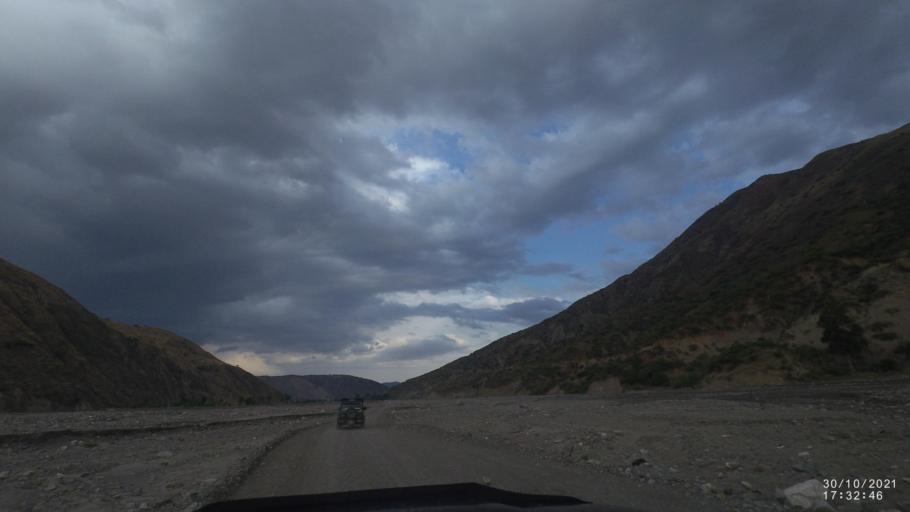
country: BO
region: Cochabamba
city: Sipe Sipe
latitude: -17.5263
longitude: -66.5855
